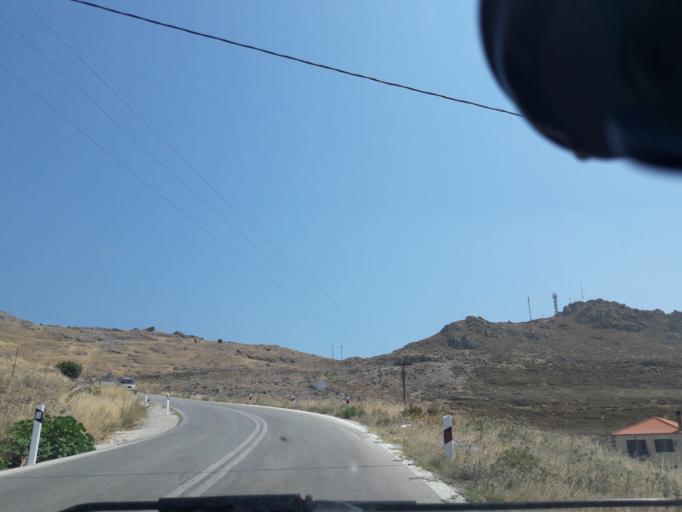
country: GR
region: North Aegean
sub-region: Nomos Lesvou
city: Myrina
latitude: 39.8640
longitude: 25.0753
